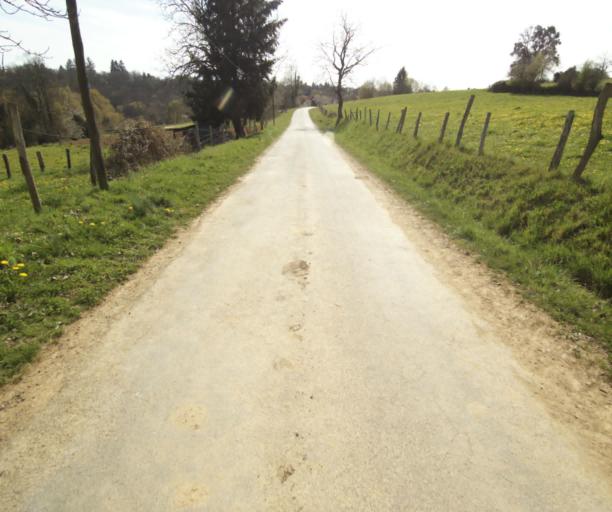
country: FR
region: Limousin
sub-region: Departement de la Correze
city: Naves
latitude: 45.3495
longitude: 1.7586
